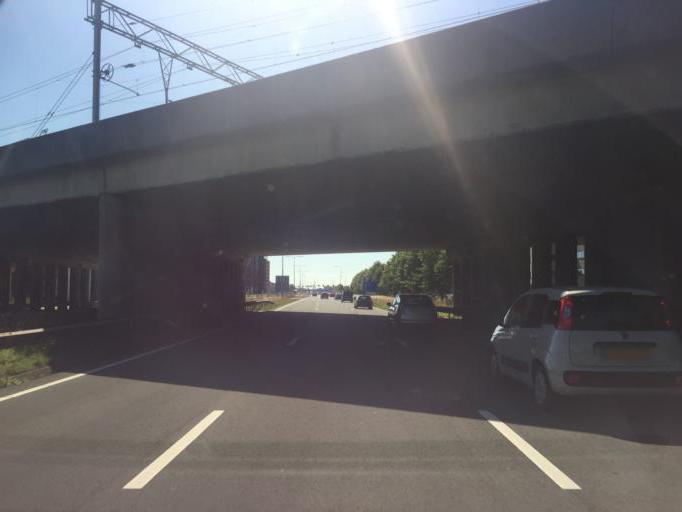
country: NL
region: North Holland
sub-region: Gemeente Haarlemmermeer
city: Hoofddorp
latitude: 52.2958
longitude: 4.7104
